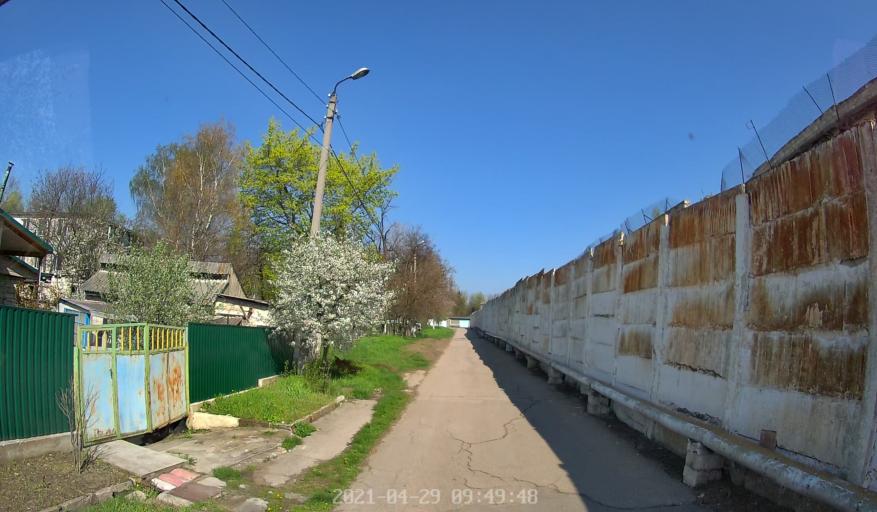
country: MD
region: Chisinau
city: Cricova
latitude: 47.1431
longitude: 28.8602
